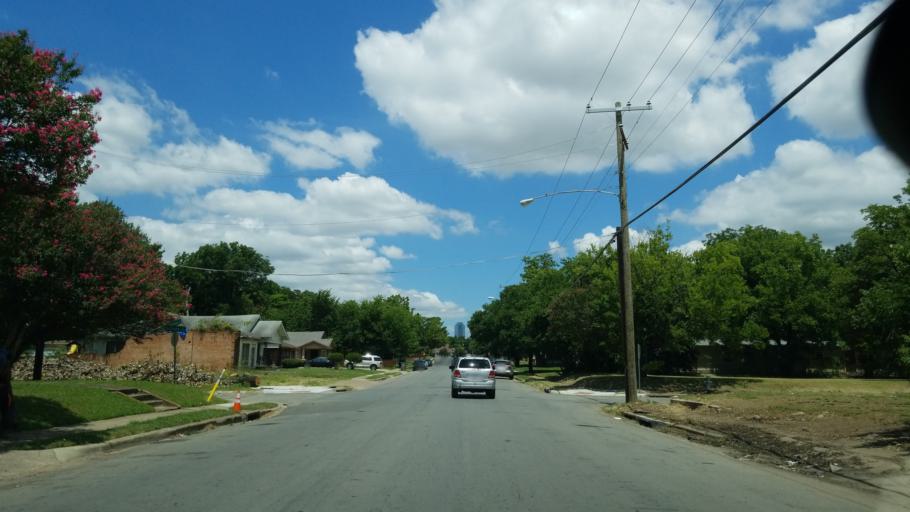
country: US
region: Texas
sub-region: Dallas County
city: Dallas
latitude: 32.7492
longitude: -96.7628
